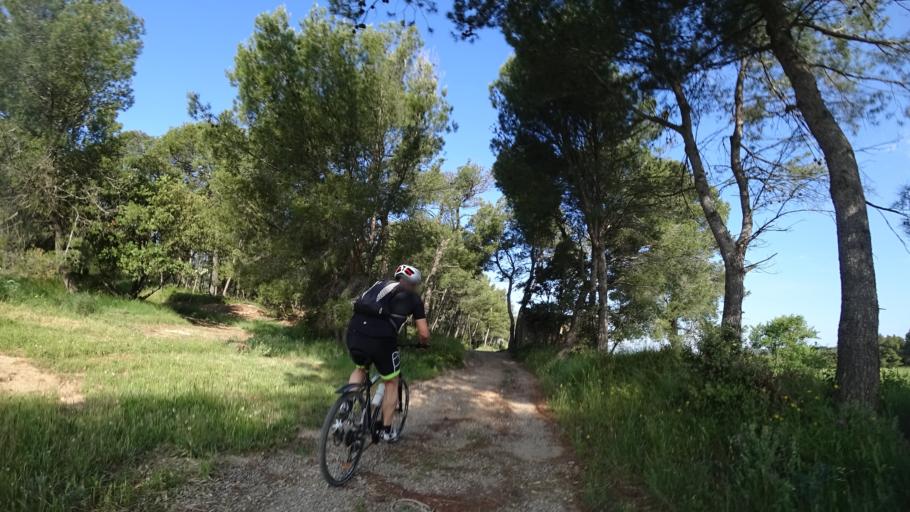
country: FR
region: Languedoc-Roussillon
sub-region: Departement de l'Aude
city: Lezignan-Corbieres
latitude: 43.2374
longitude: 2.7411
